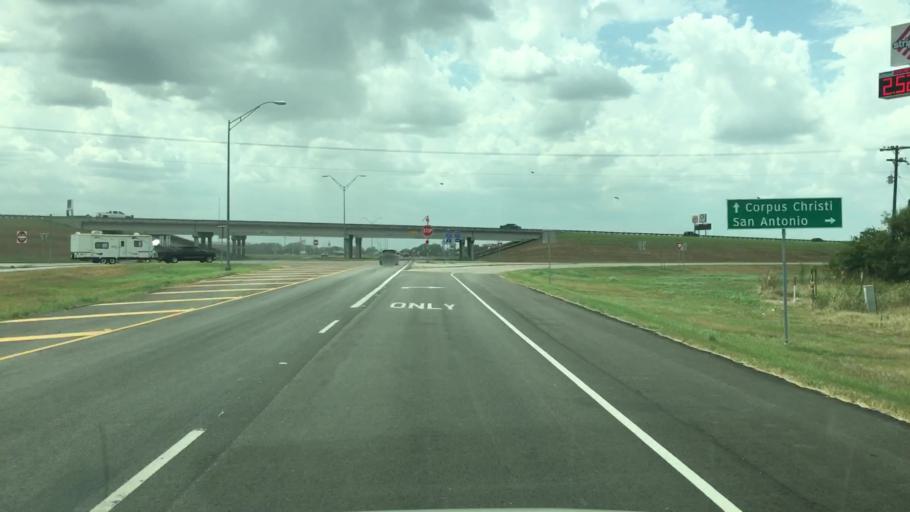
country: US
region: Texas
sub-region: Live Oak County
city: George West
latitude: 28.3380
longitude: -98.0247
